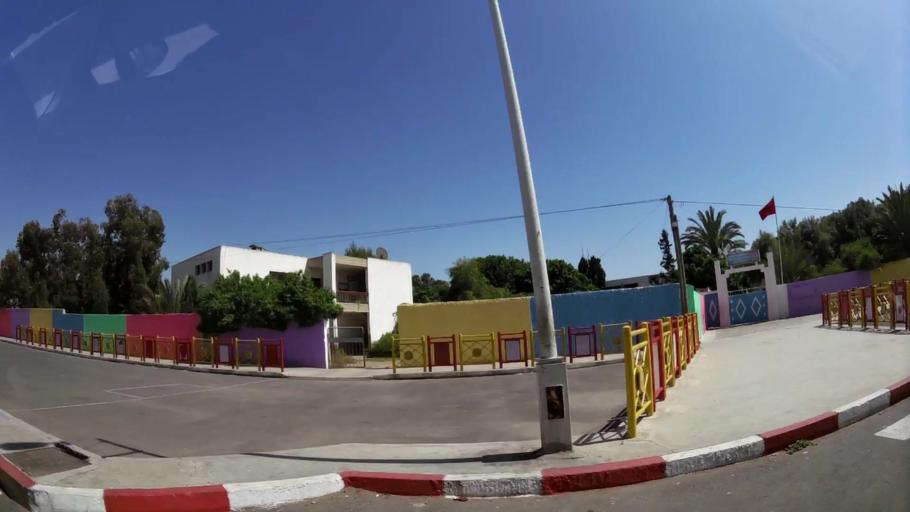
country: MA
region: Souss-Massa-Draa
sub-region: Agadir-Ida-ou-Tnan
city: Agadir
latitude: 30.4108
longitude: -9.5853
